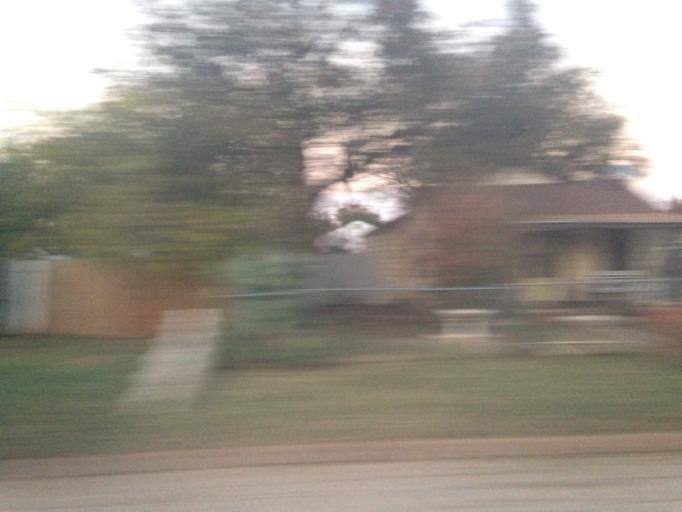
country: US
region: Texas
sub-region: Taylor County
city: Abilene
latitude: 32.4474
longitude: -99.7571
